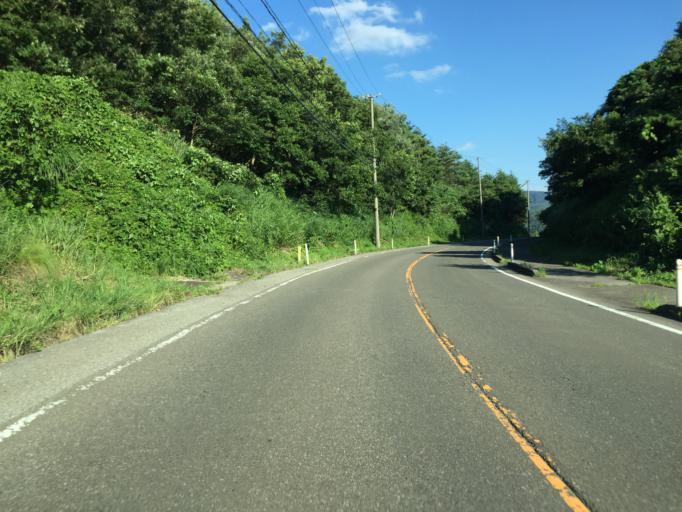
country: JP
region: Miyagi
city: Shiroishi
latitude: 37.9865
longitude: 140.4585
